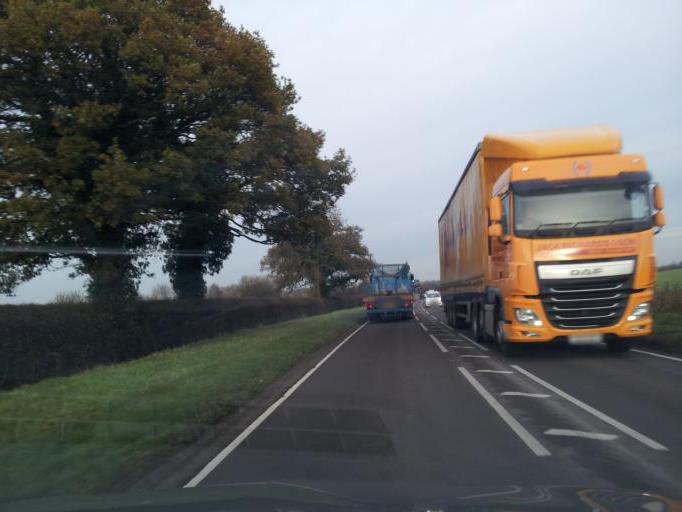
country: GB
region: England
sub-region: Buckinghamshire
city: Stewkley
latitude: 51.8791
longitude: -0.7420
